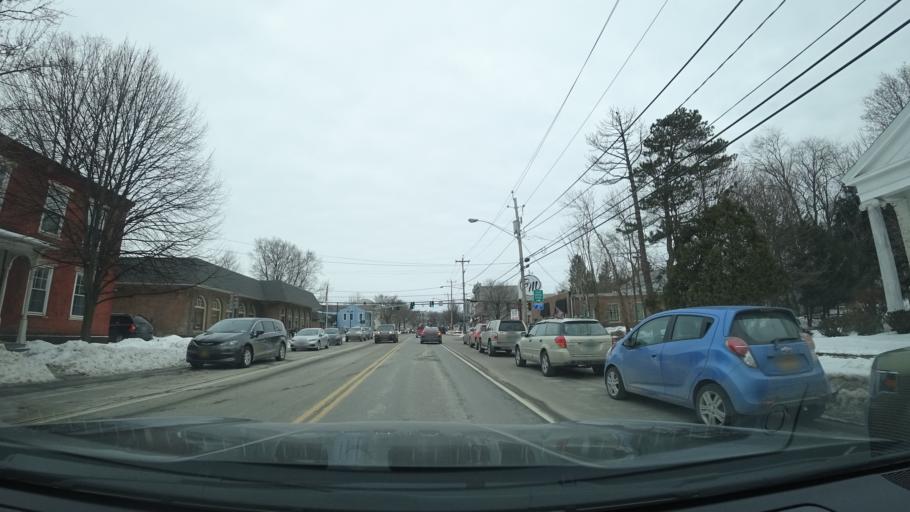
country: US
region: New York
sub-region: Washington County
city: Cambridge
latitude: 43.1718
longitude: -73.3273
